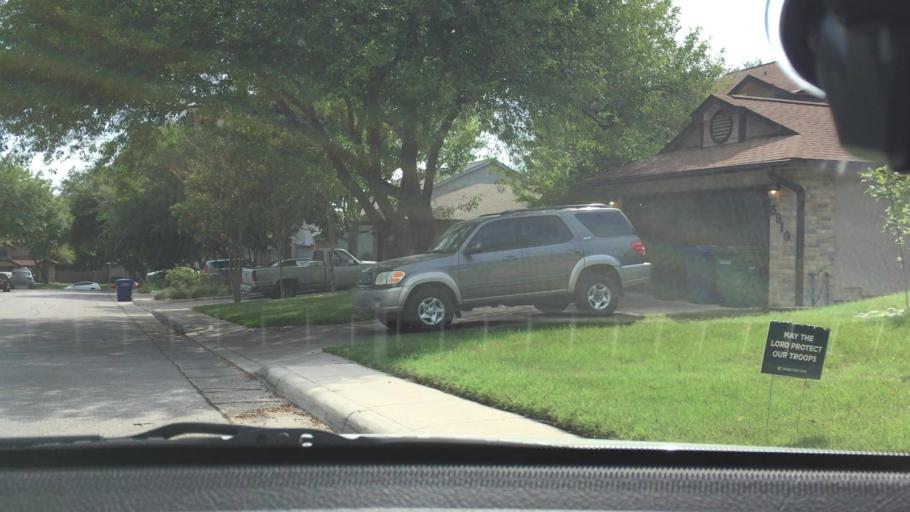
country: US
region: Texas
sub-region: Bexar County
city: Live Oak
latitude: 29.5798
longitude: -98.3783
